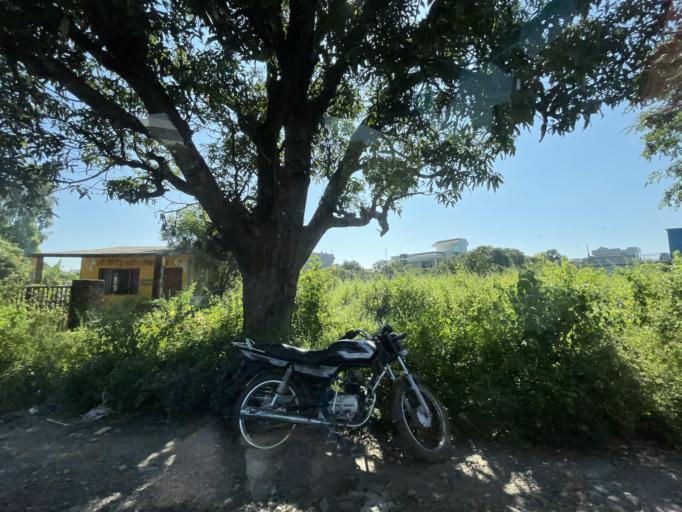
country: IN
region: Uttarakhand
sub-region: Naini Tal
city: Haldwani
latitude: 29.2112
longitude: 79.4690
